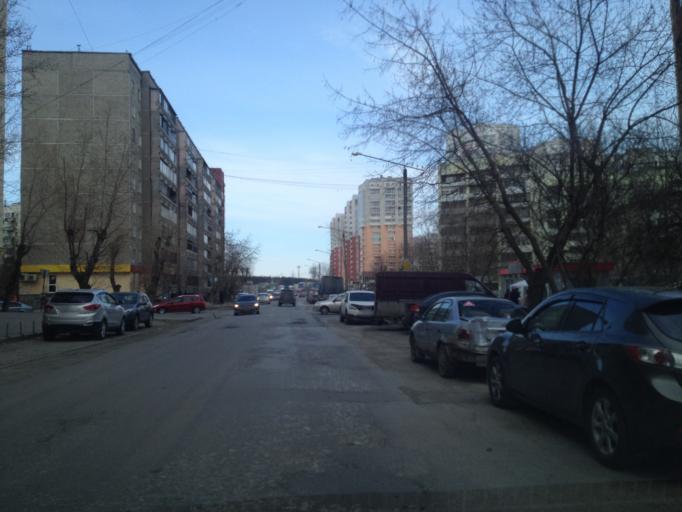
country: RU
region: Sverdlovsk
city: Yekaterinburg
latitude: 56.9064
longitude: 60.6175
